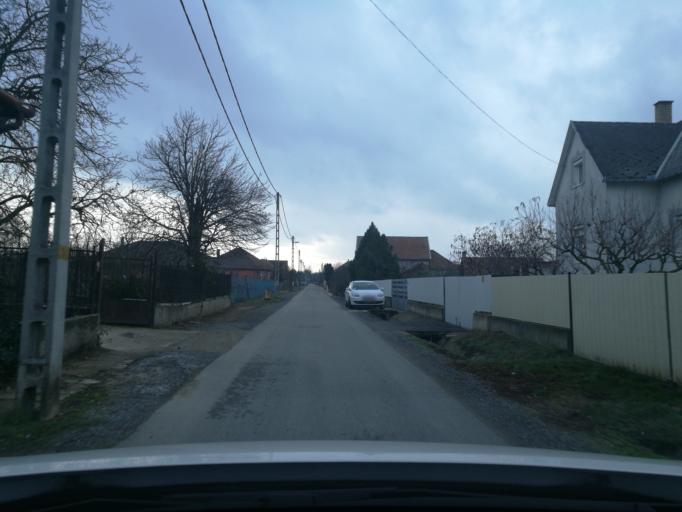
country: HU
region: Szabolcs-Szatmar-Bereg
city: Nyirpazony
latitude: 47.9807
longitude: 21.7876
